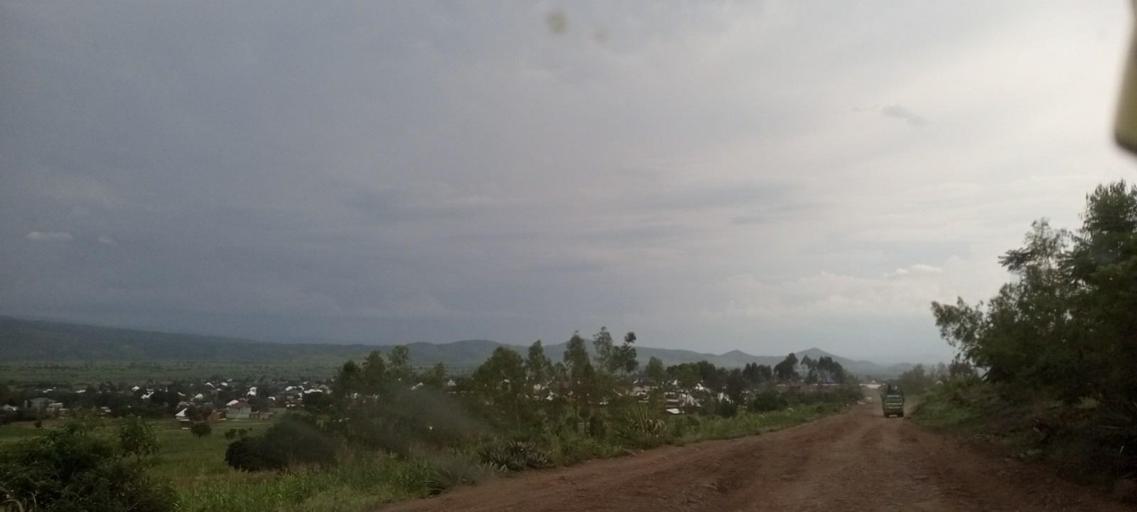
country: BI
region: Cibitoke
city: Cibitoke
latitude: -2.7221
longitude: 28.9988
